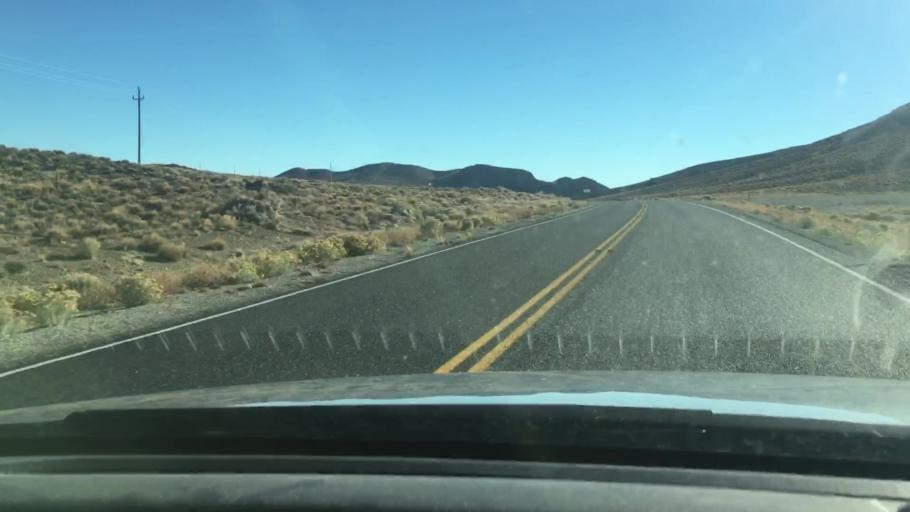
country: US
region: Nevada
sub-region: Nye County
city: Tonopah
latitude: 38.1124
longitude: -116.9061
